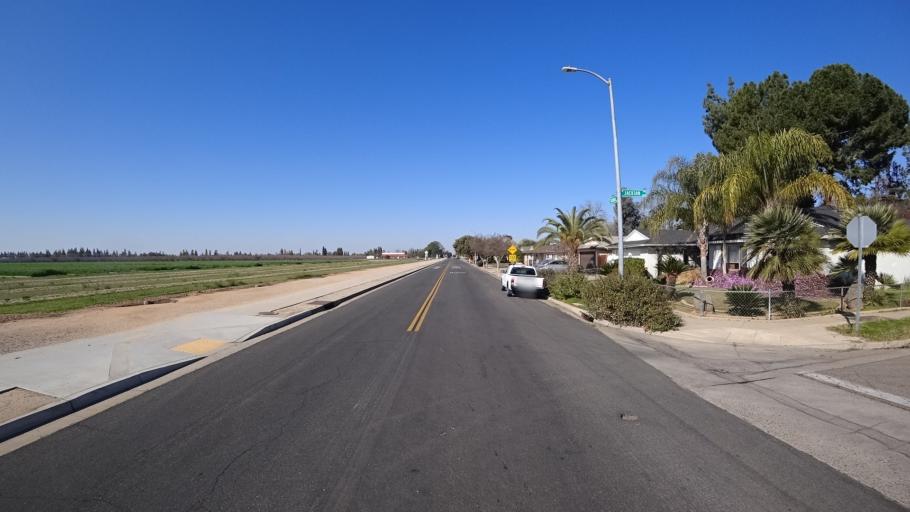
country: US
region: California
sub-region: Fresno County
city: Clovis
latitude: 36.8303
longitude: -119.7474
